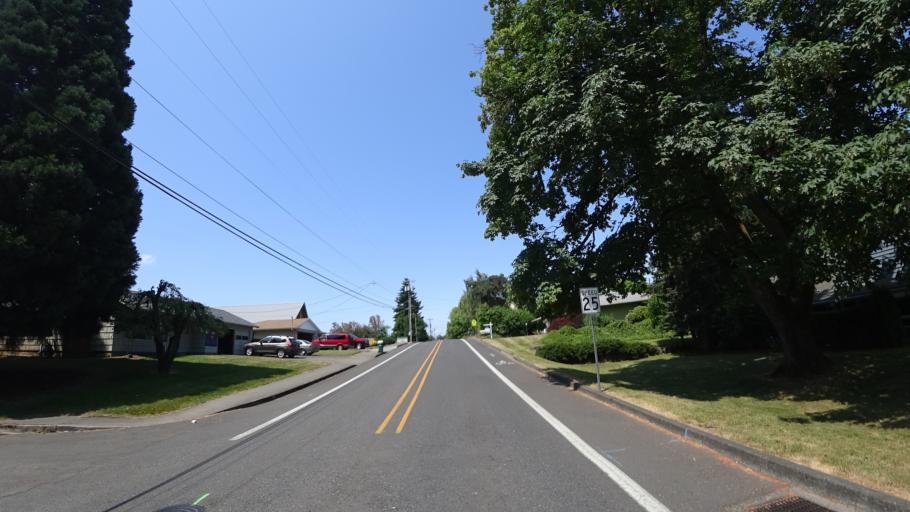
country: US
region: Oregon
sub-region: Clackamas County
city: Oatfield
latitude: 45.4434
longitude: -122.5843
